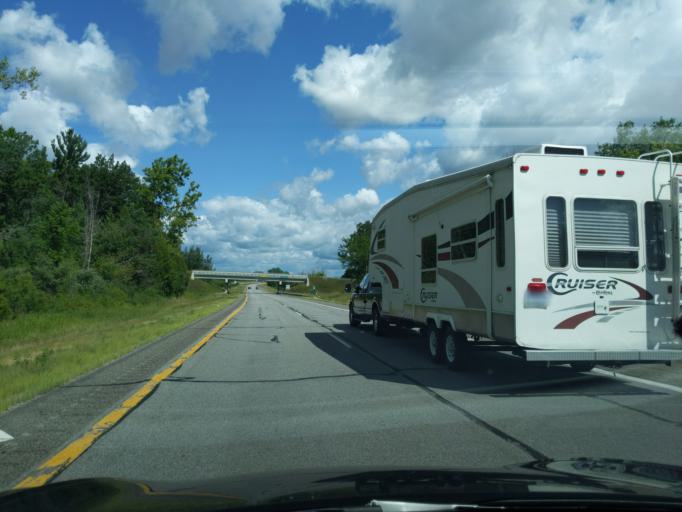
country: US
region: Michigan
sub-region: Clare County
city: Clare
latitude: 43.7551
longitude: -84.7572
